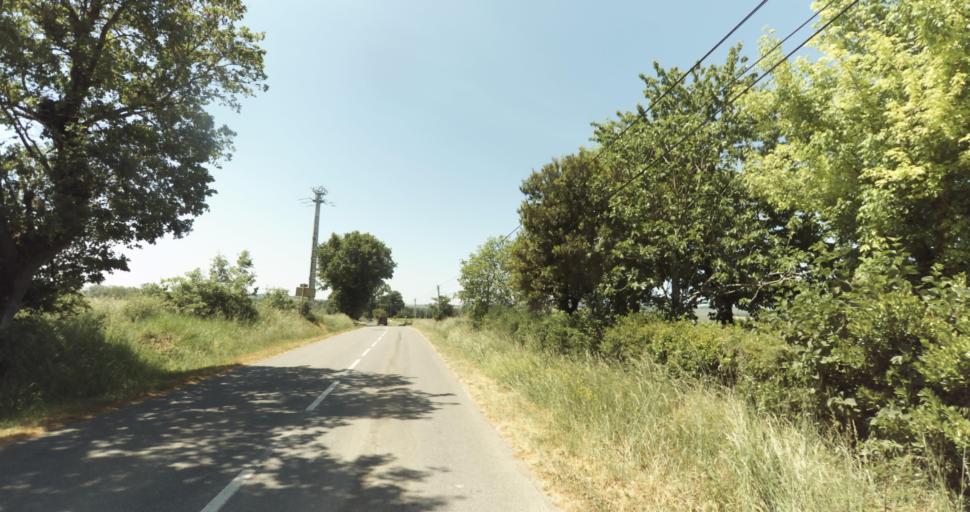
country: FR
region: Midi-Pyrenees
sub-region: Departement de la Haute-Garonne
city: Levignac
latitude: 43.6408
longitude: 1.1639
